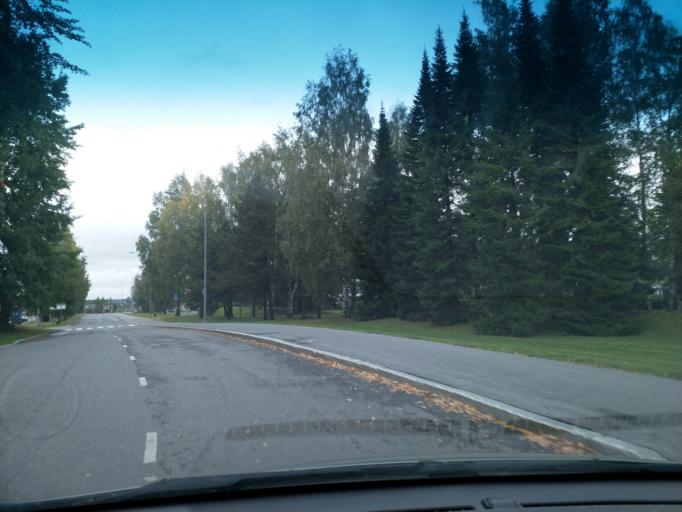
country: FI
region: Pirkanmaa
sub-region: Tampere
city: Tampere
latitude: 61.4760
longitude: 23.8425
